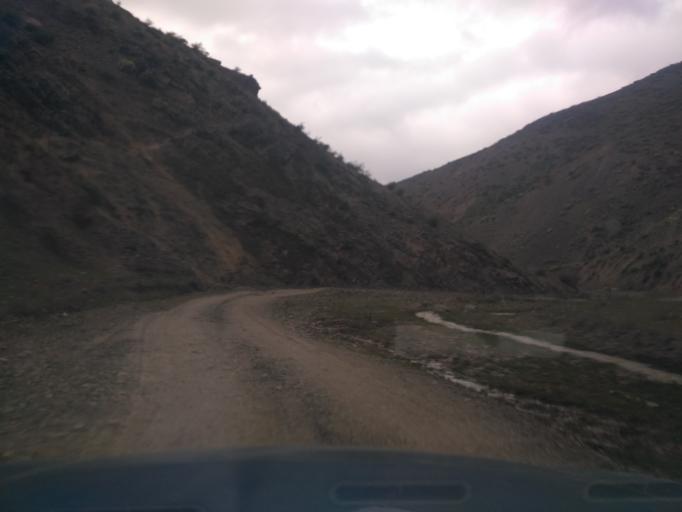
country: UZ
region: Jizzax
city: Zomin
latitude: 39.8593
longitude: 68.3850
